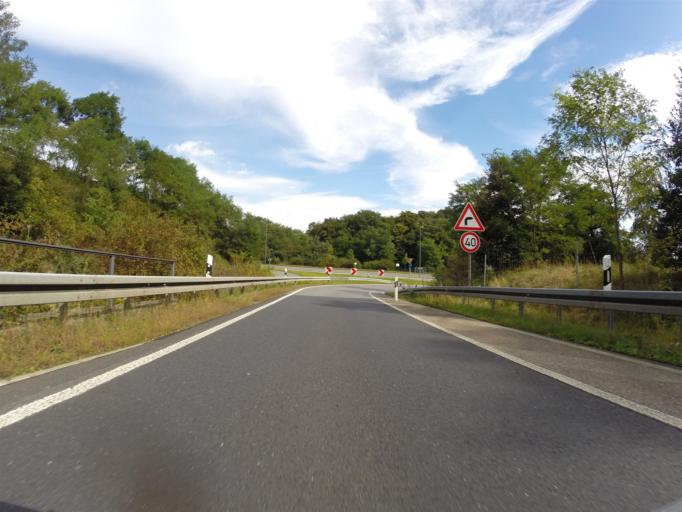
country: DE
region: Saxony
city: Albertstadt
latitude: 51.1066
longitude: 13.7338
